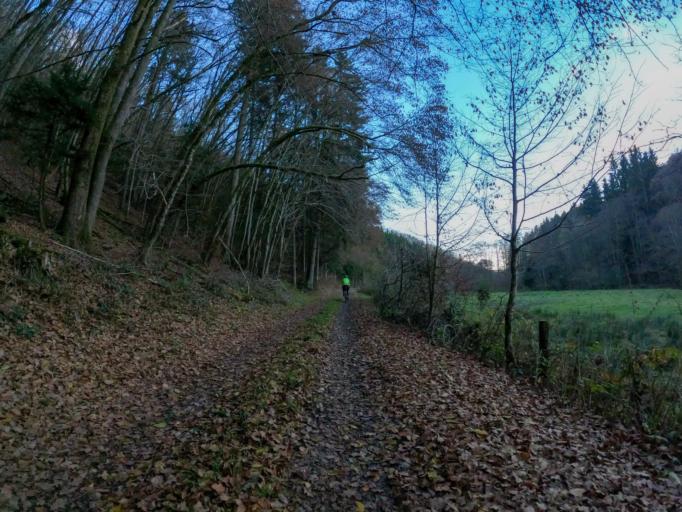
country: LU
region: Diekirch
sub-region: Canton de Wiltz
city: Bavigne
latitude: 49.9362
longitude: 5.8409
